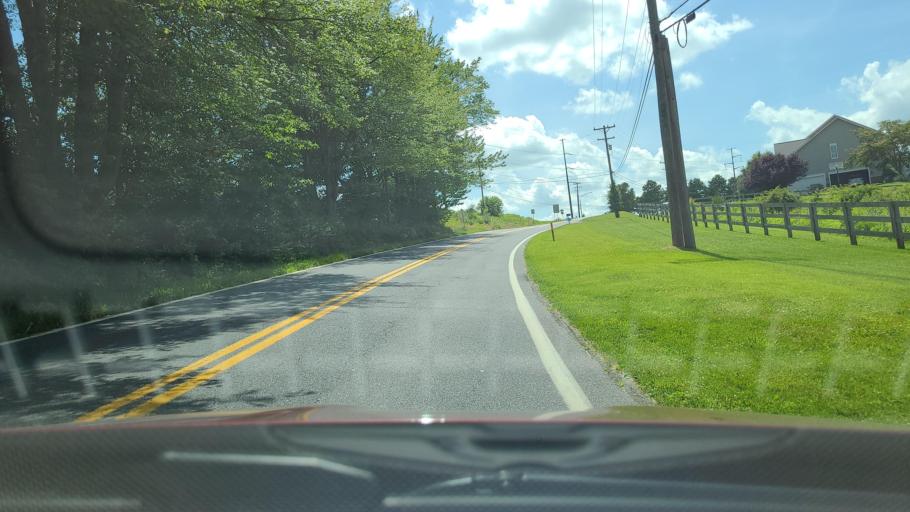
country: US
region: Maryland
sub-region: Montgomery County
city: Clarksburg
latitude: 39.2492
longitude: -77.2724
